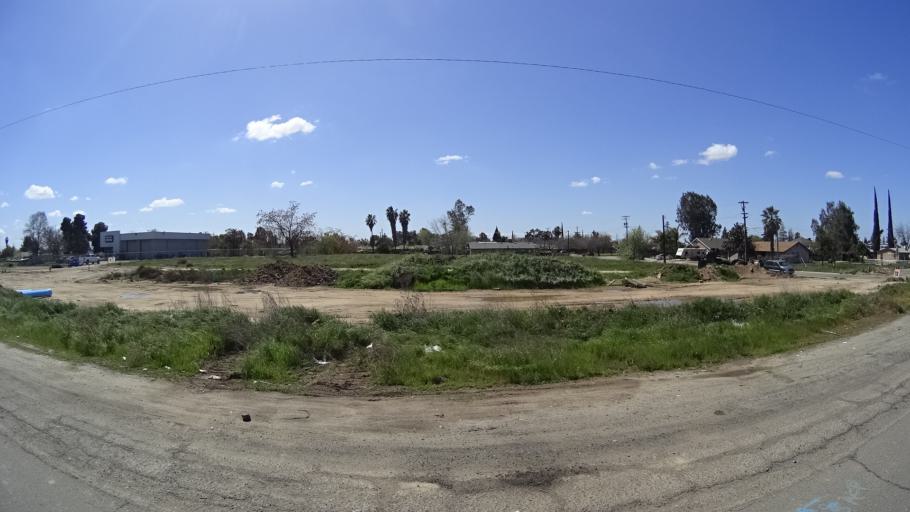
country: US
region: California
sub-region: Fresno County
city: West Park
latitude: 36.8137
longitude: -119.8851
